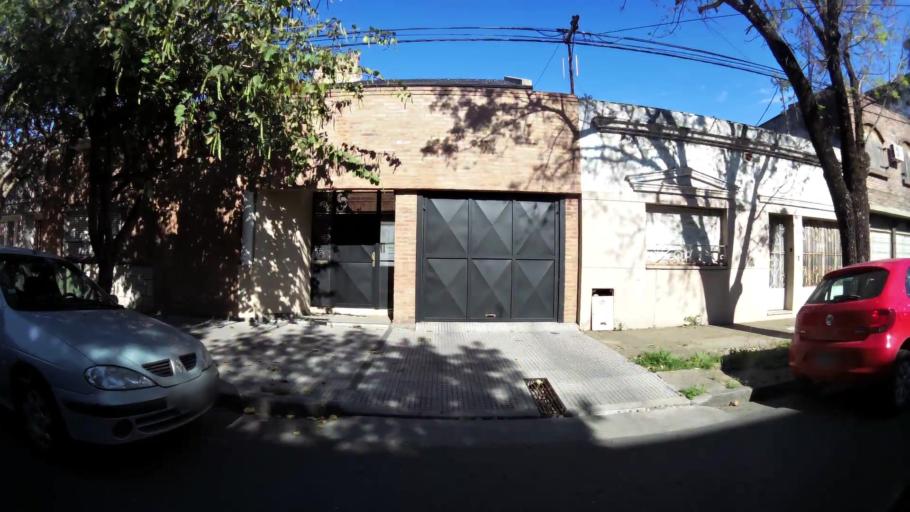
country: AR
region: Santa Fe
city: Santa Fe de la Vera Cruz
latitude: -31.6382
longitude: -60.7151
